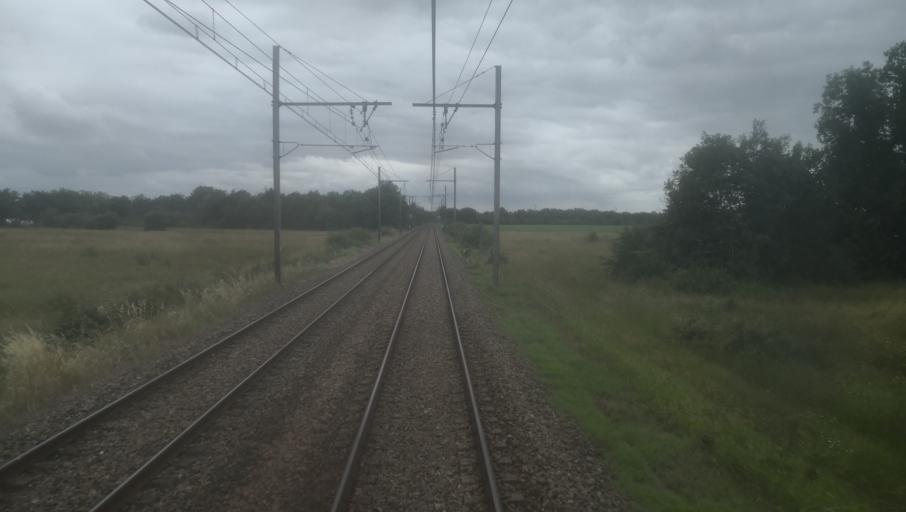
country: FR
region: Midi-Pyrenees
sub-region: Departement du Tarn-et-Garonne
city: Saint-Porquier
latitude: 44.0362
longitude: 1.1904
